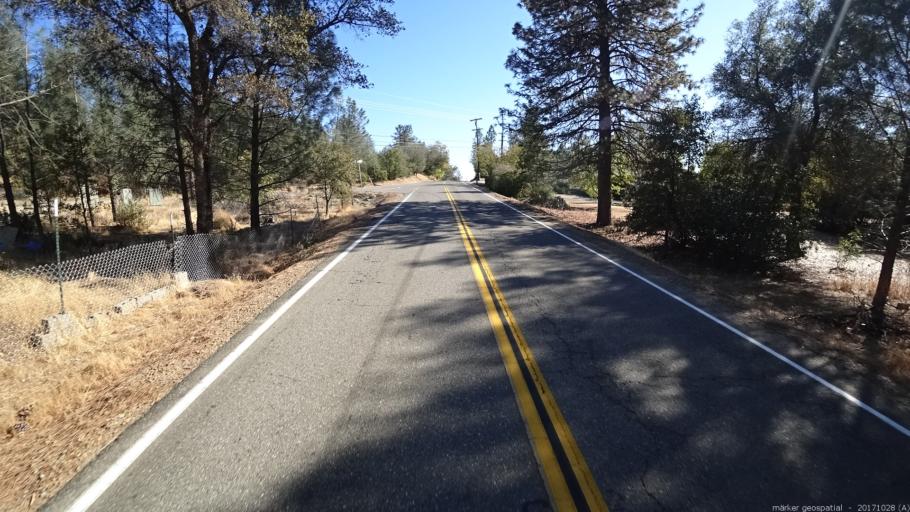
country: US
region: California
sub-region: Shasta County
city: Shasta
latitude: 40.6199
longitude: -122.4640
